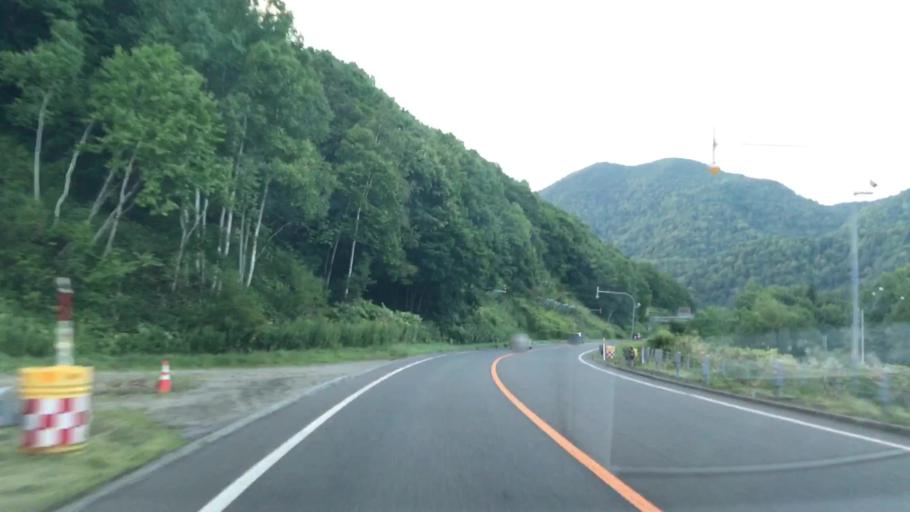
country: JP
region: Hokkaido
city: Sapporo
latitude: 42.9113
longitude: 141.1200
